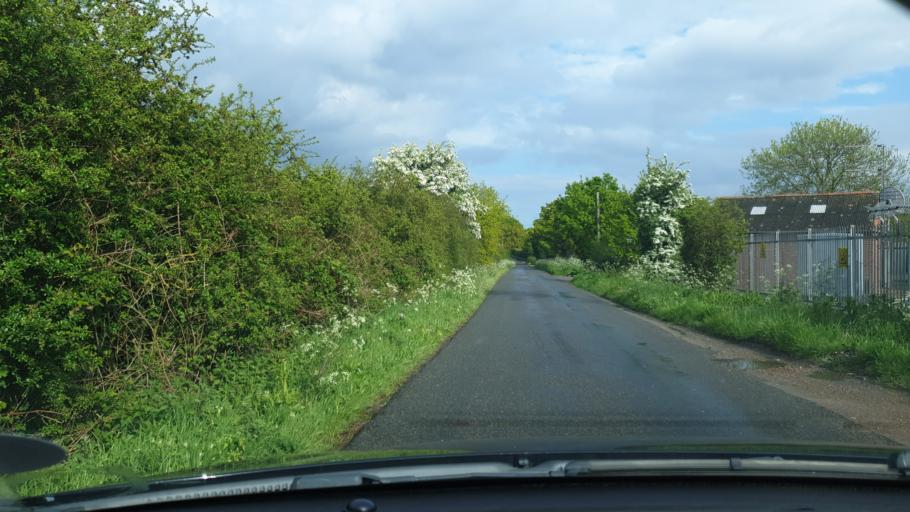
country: GB
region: England
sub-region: Essex
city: Saint Osyth
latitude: 51.8256
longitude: 1.0926
